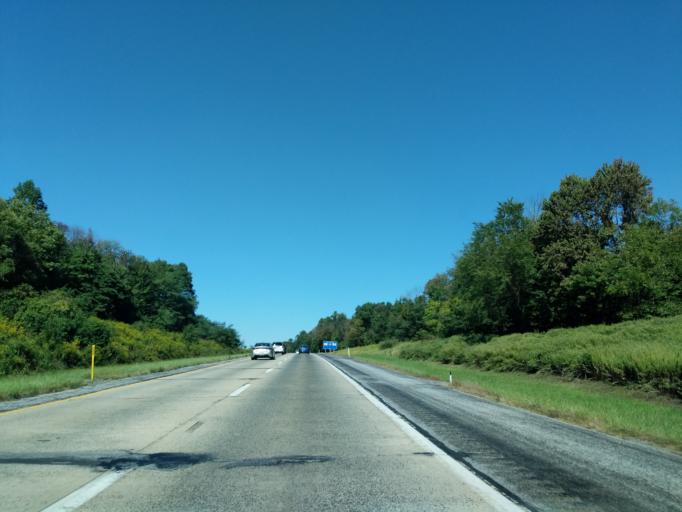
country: US
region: Pennsylvania
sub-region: Montgomery County
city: Audubon
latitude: 40.1501
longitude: -75.4597
